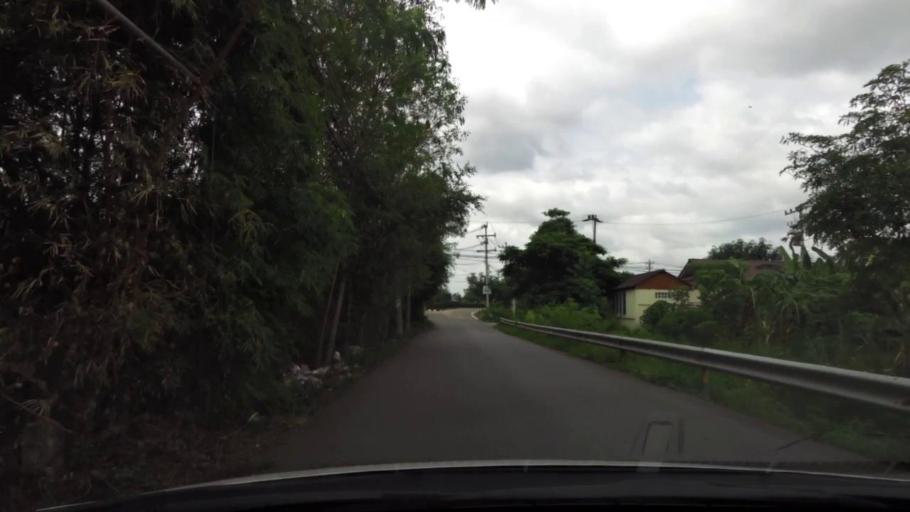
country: TH
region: Ratchaburi
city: Ratchaburi
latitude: 13.5271
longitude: 99.8328
